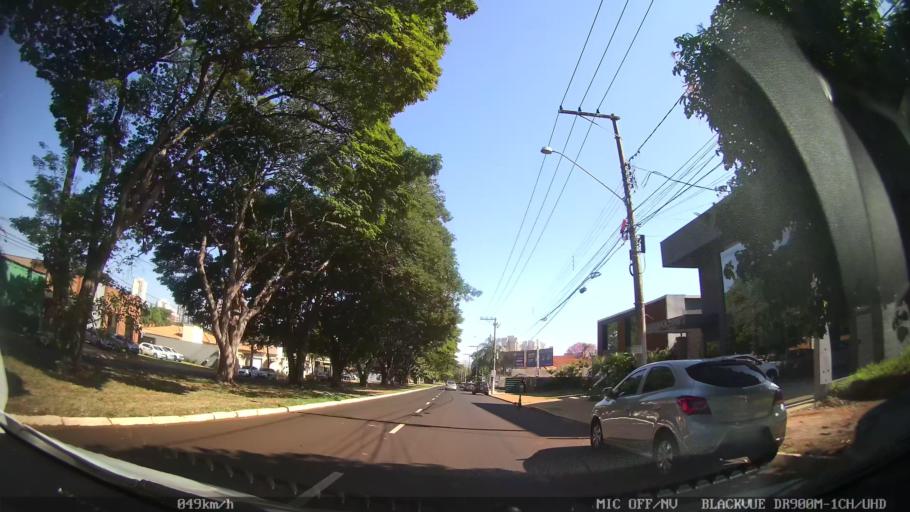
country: BR
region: Sao Paulo
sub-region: Ribeirao Preto
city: Ribeirao Preto
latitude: -21.2191
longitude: -47.8123
